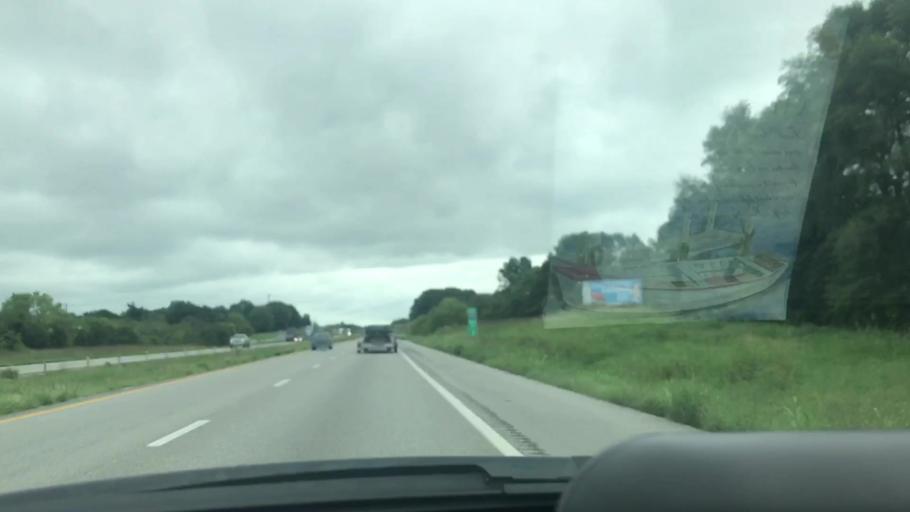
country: US
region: Missouri
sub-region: Greene County
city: Springfield
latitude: 37.2499
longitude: -93.3246
